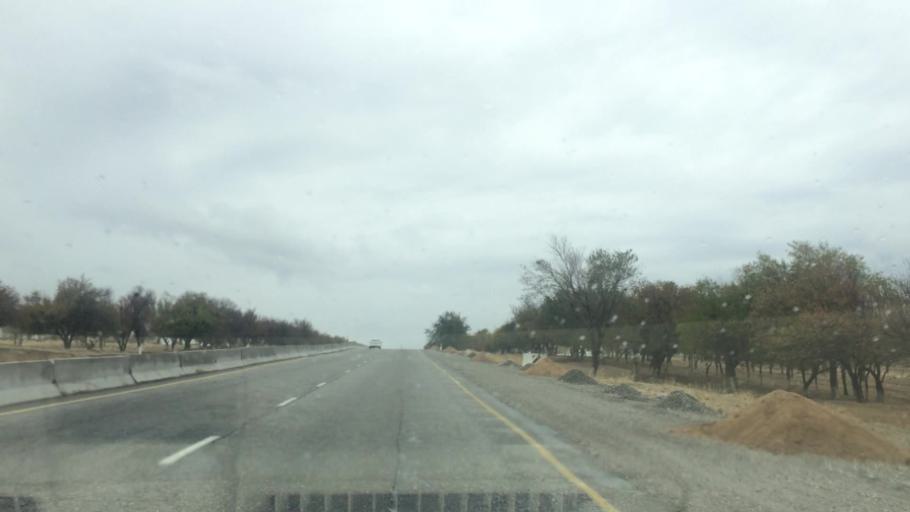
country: UZ
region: Samarqand
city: Bulung'ur
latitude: 39.8601
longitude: 67.4697
